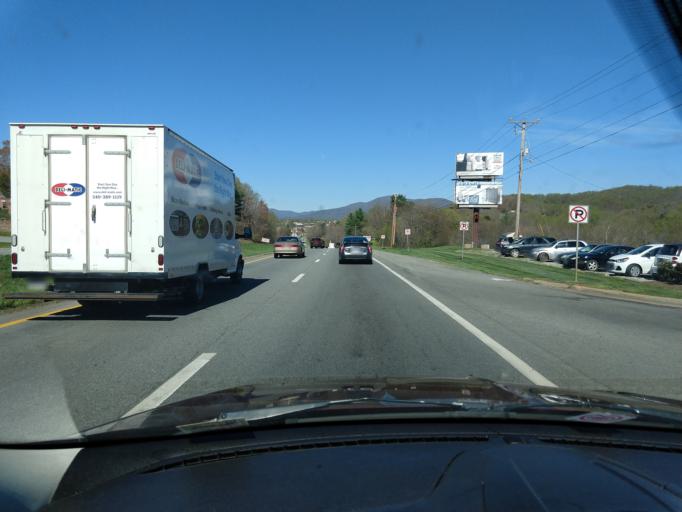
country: US
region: Virginia
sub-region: Franklin County
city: Rocky Mount
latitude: 37.0720
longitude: -79.8986
